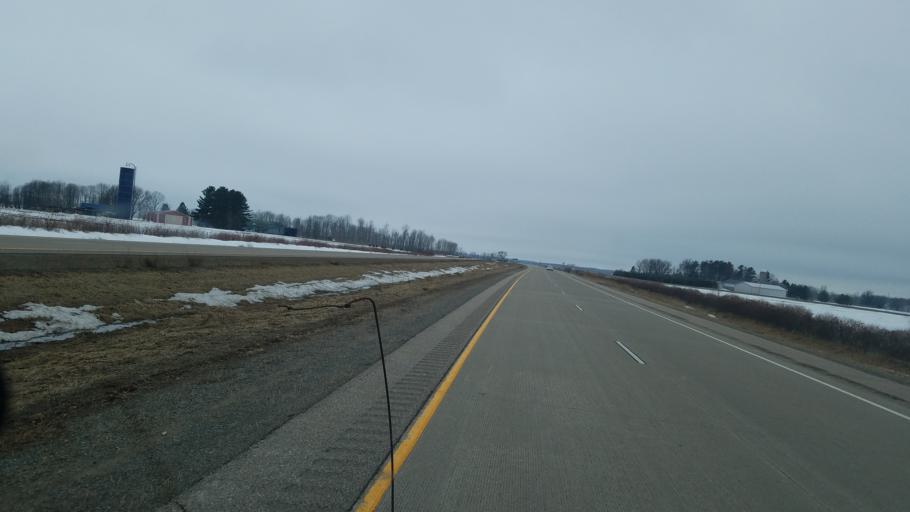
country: US
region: Wisconsin
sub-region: Wood County
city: Wisconsin Rapids
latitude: 44.6095
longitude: -89.8391
